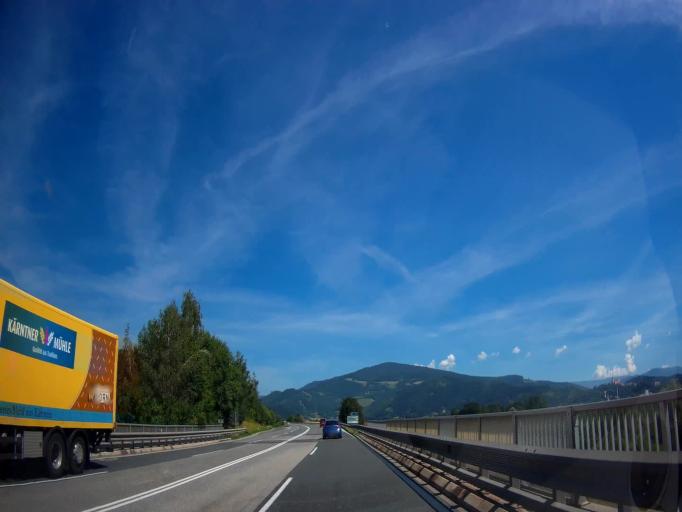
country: AT
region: Carinthia
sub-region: Politischer Bezirk Sankt Veit an der Glan
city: Molbling
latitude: 46.8593
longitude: 14.4495
